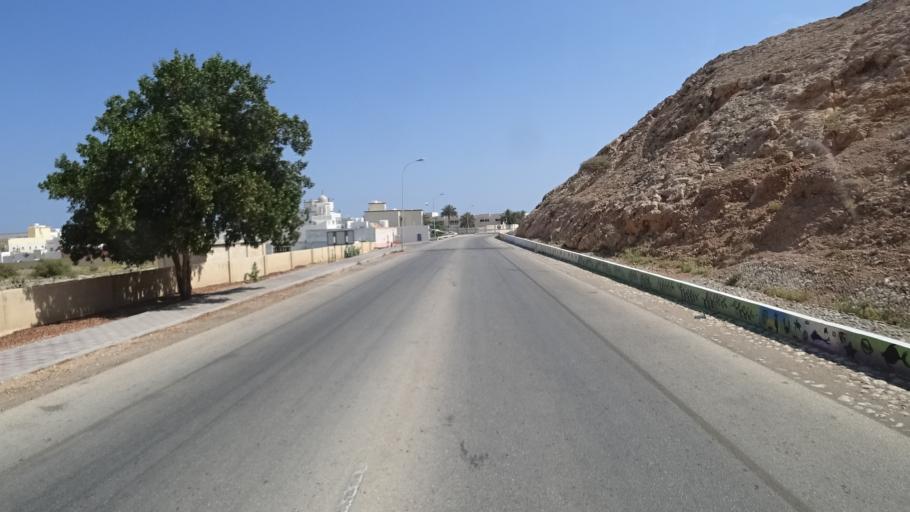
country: OM
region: Ash Sharqiyah
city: Sur
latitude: 22.5645
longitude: 59.5473
